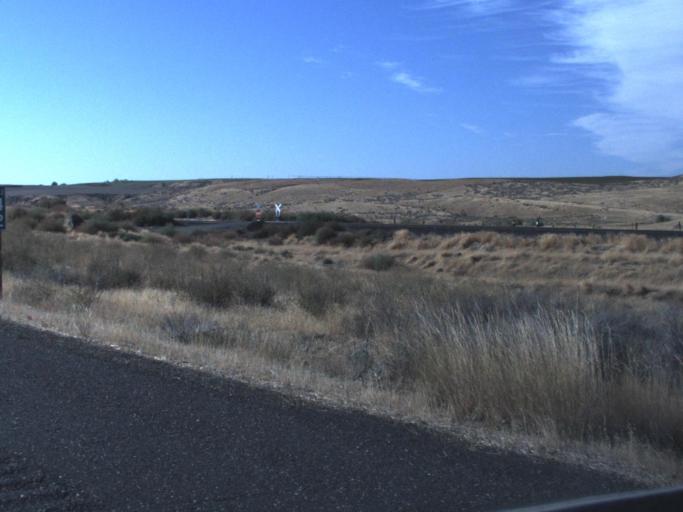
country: US
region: Washington
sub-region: Franklin County
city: Basin City
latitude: 46.5140
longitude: -119.0140
